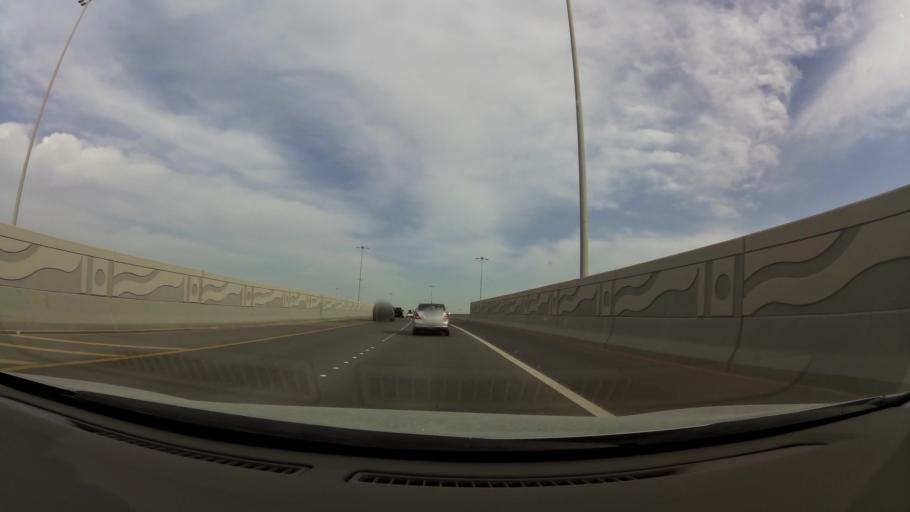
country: QA
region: Baladiyat ad Dawhah
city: Doha
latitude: 25.2557
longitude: 51.5042
